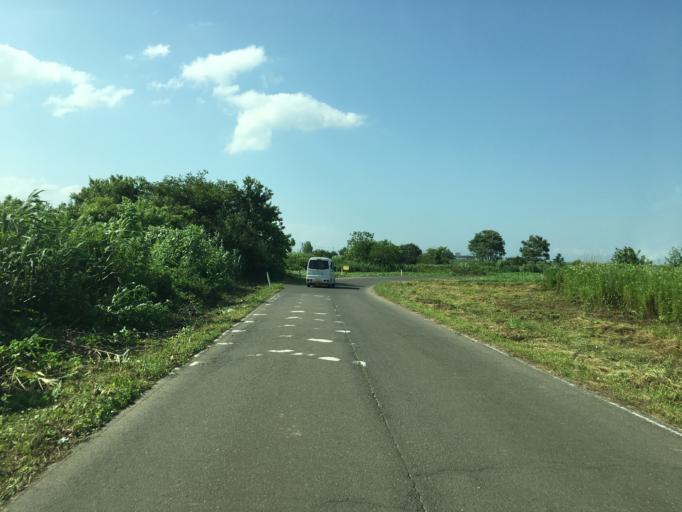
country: JP
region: Miyagi
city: Kakuda
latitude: 37.9644
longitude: 140.7885
